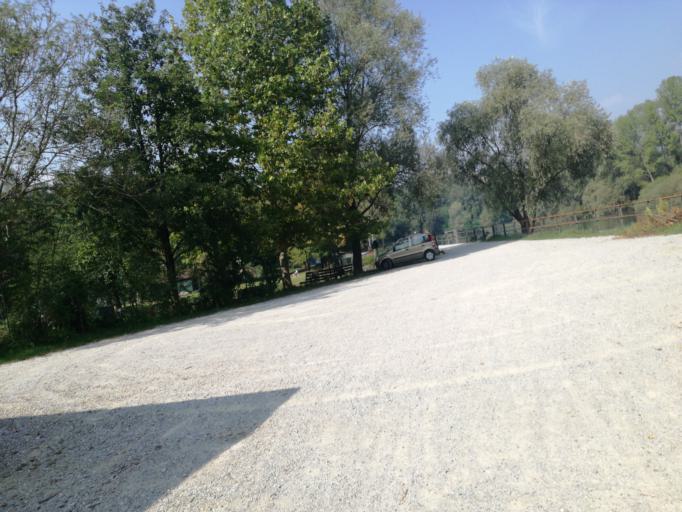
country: IT
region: Lombardy
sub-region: Provincia di Lecco
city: Brivio
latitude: 45.7308
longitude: 9.4463
